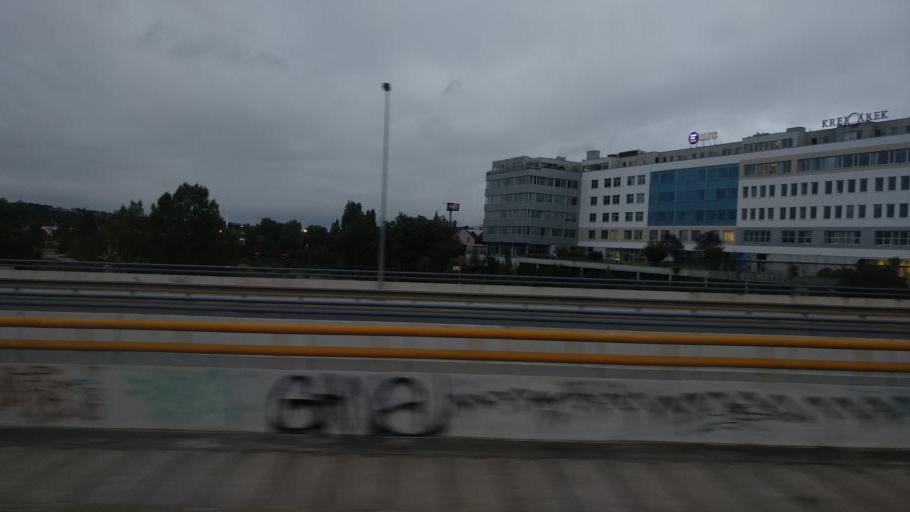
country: CZ
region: Praha
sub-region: Praha 8
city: Liben
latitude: 50.0968
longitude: 14.4751
